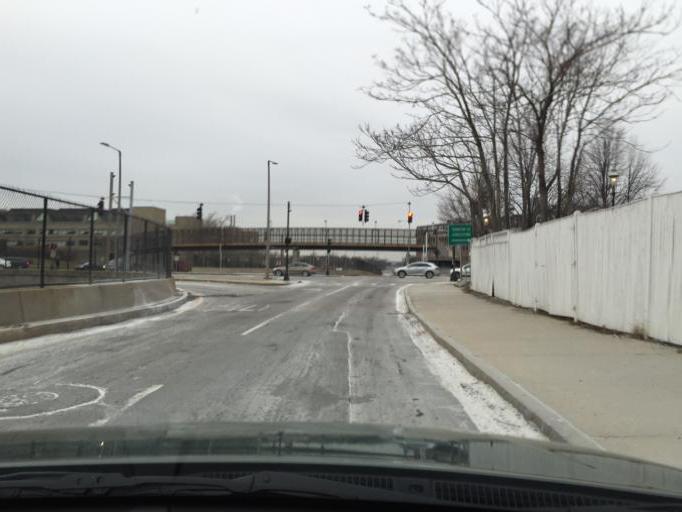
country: US
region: Massachusetts
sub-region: Suffolk County
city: Boston
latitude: 42.3739
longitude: -71.0672
